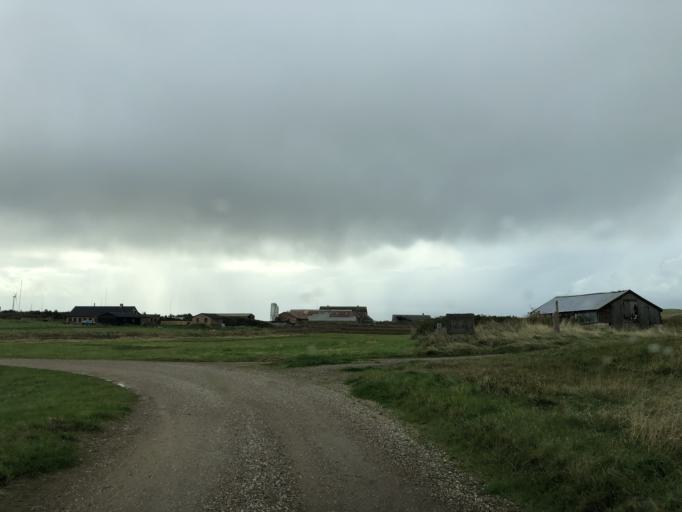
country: DK
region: Central Jutland
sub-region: Lemvig Kommune
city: Harboore
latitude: 56.4630
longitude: 8.1296
